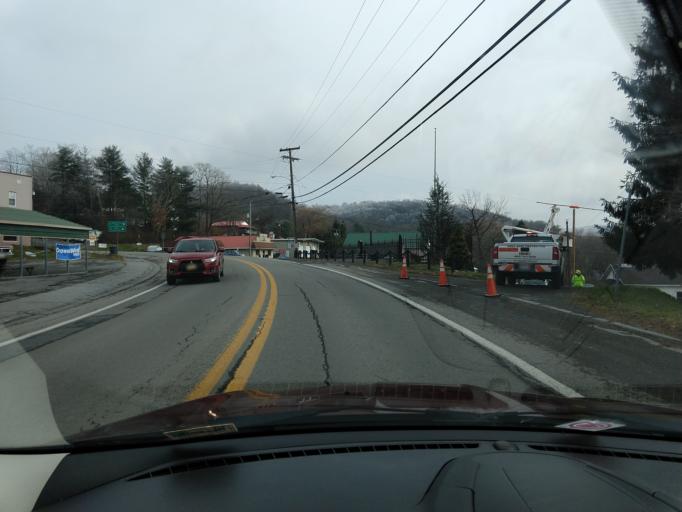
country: US
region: West Virginia
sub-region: Greenbrier County
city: Rainelle
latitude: 38.0570
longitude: -80.7073
